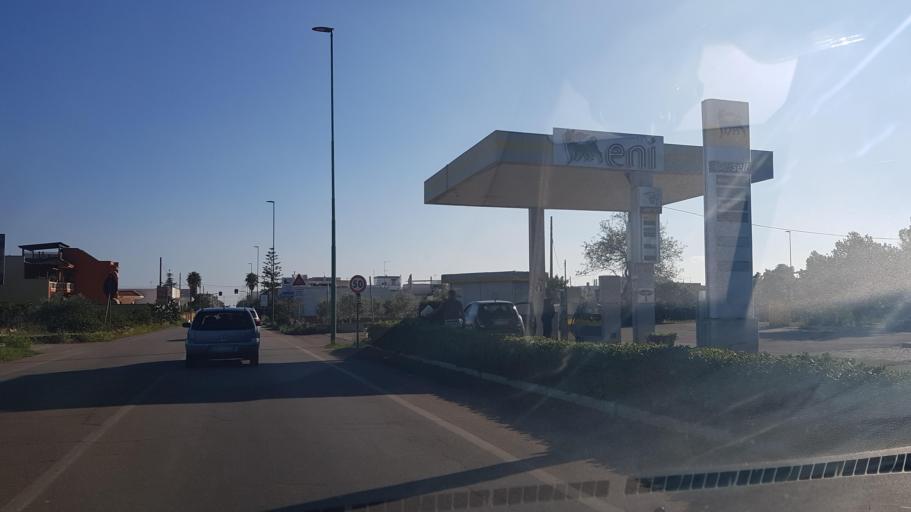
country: IT
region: Apulia
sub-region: Provincia di Lecce
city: Montesano Salentino
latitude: 39.9817
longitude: 18.3234
